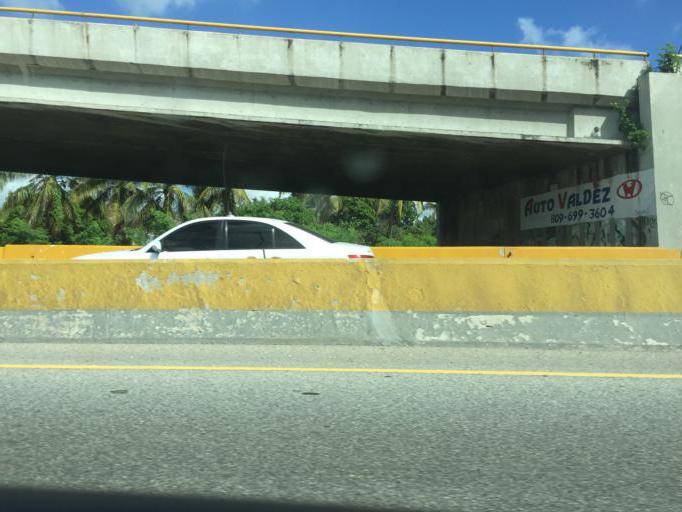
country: DO
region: Santo Domingo
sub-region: Santo Domingo
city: Santo Domingo Este
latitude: 18.4815
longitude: -69.8401
